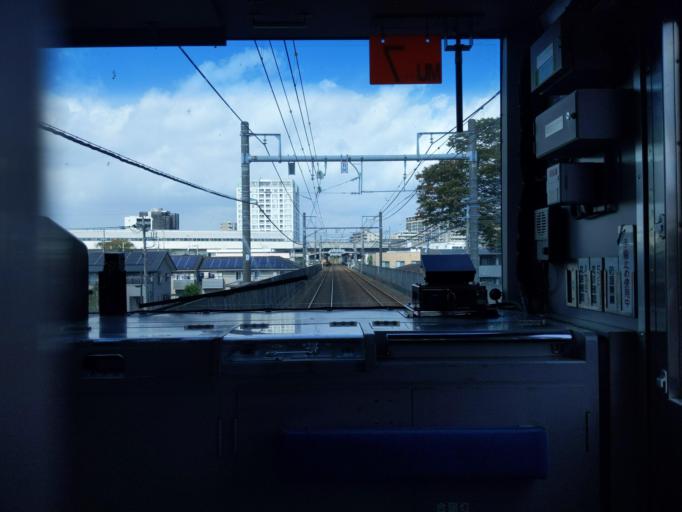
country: JP
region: Chiba
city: Matsudo
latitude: 35.7681
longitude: 139.9448
